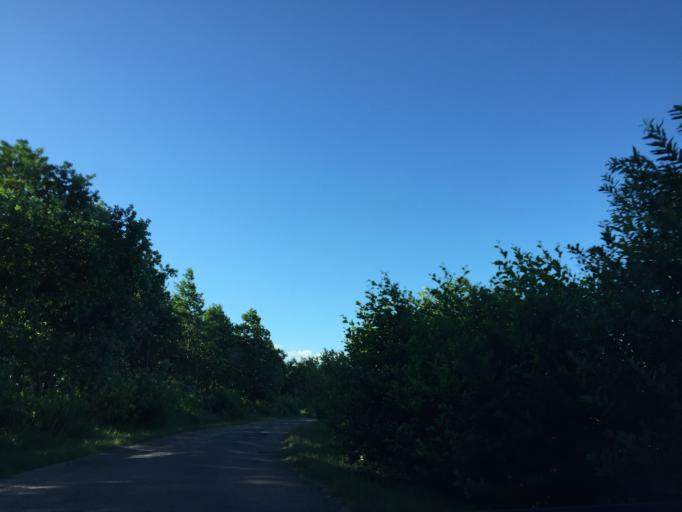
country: LV
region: Ventspils
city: Ventspils
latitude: 57.4065
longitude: 21.6475
